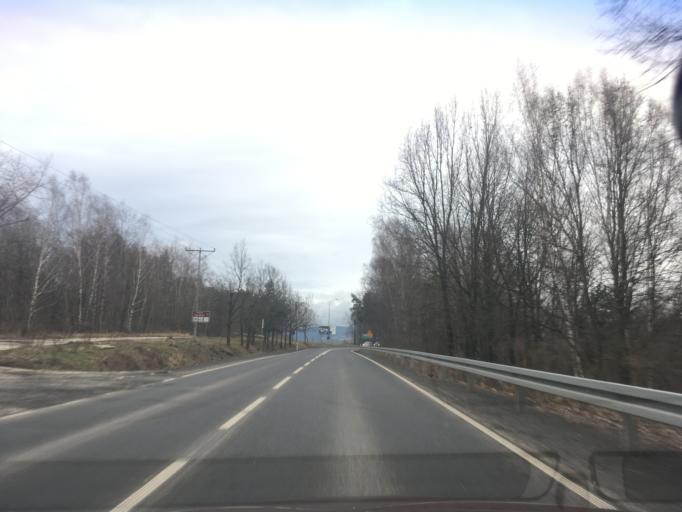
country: PL
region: Lower Silesian Voivodeship
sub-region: Powiat zgorzelecki
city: Bogatynia
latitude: 50.9234
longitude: 14.9449
